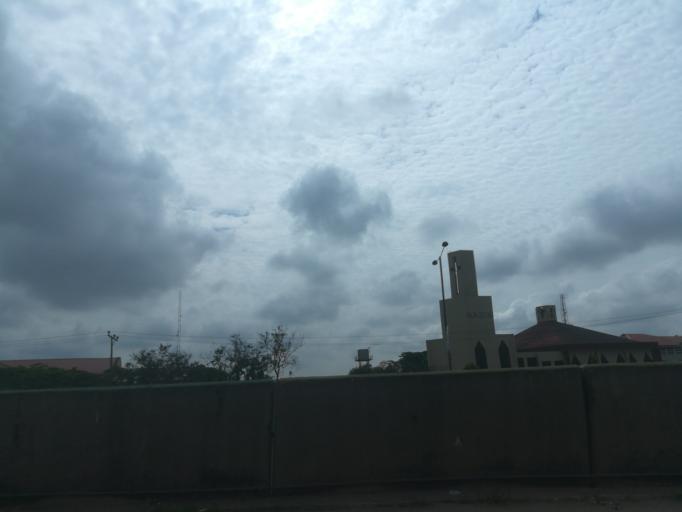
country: NG
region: Lagos
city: Ojota
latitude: 6.5704
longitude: 3.3670
